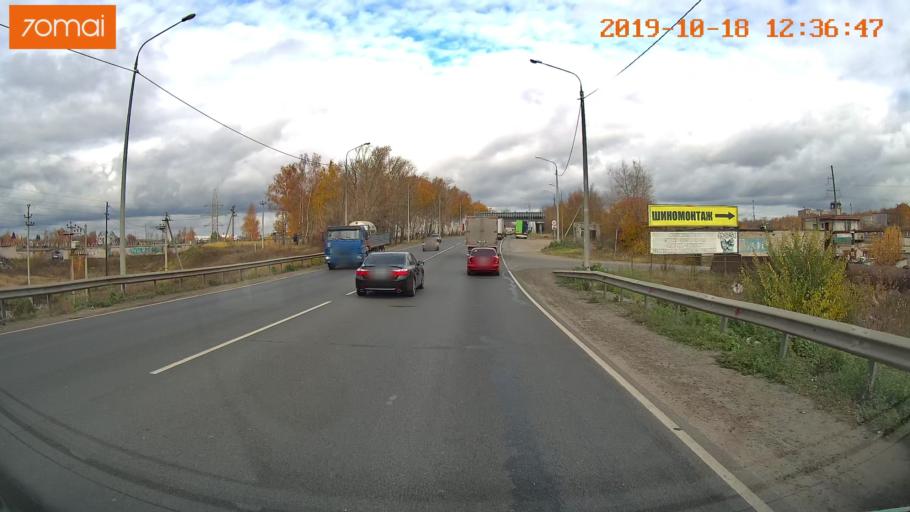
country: RU
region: Rjazan
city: Ryazan'
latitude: 54.6382
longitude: 39.6351
